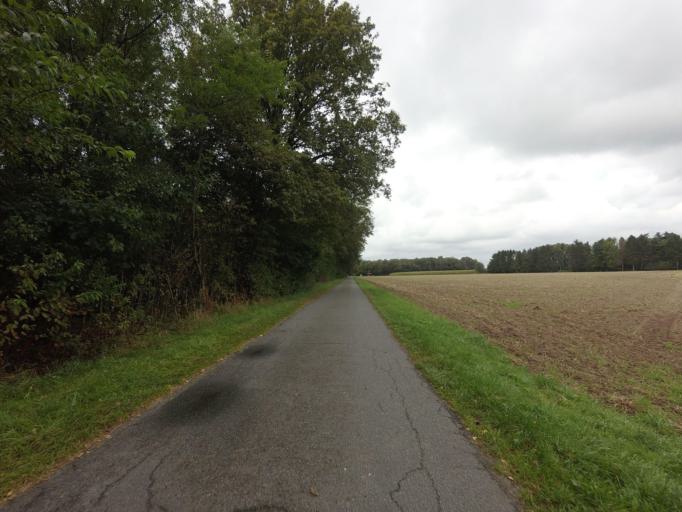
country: DE
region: North Rhine-Westphalia
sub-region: Regierungsbezirk Munster
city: Gronau
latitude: 52.2538
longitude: 7.0774
